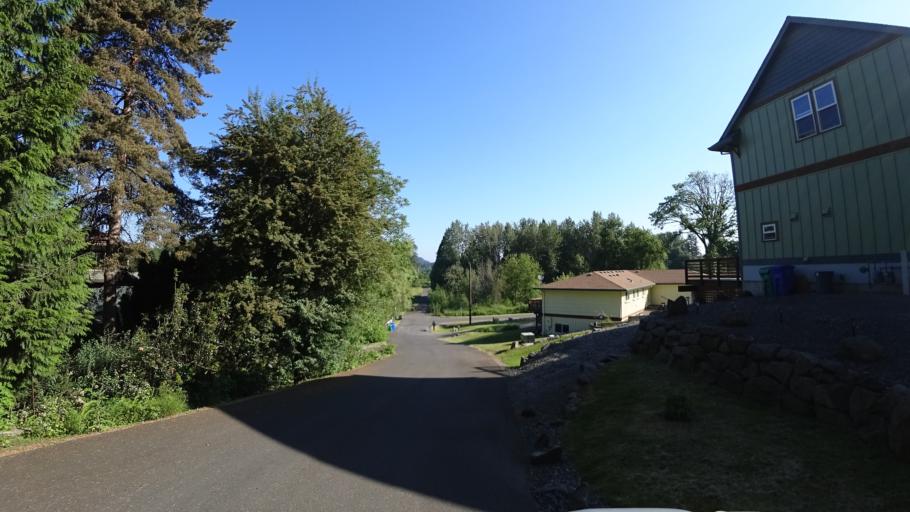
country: US
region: Oregon
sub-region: Multnomah County
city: Lents
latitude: 45.4720
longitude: -122.5519
